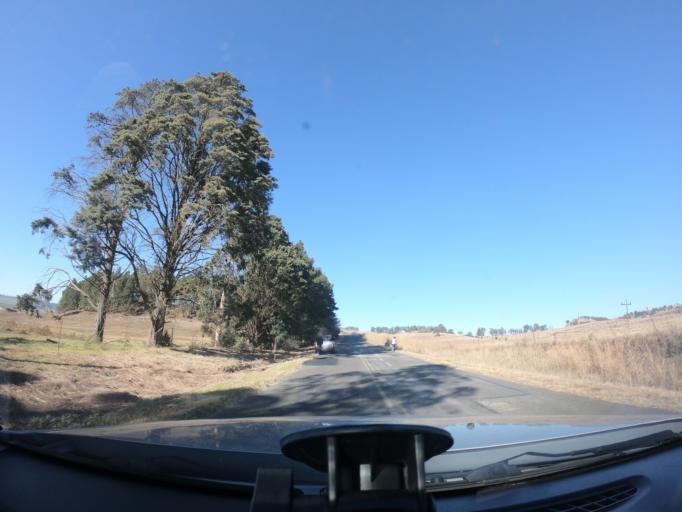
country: ZA
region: KwaZulu-Natal
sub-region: uMgungundlovu District Municipality
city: Mooirivier
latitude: -29.3188
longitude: 29.9211
